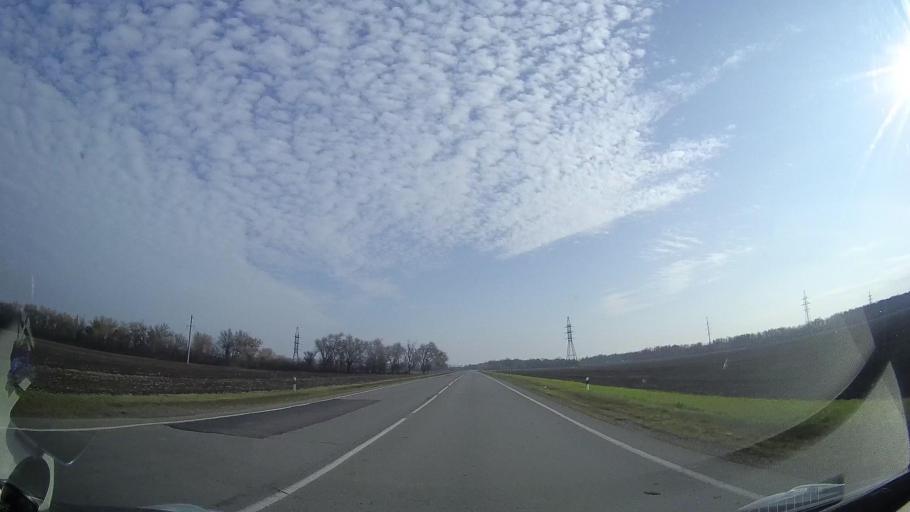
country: RU
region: Rostov
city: Tselina
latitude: 46.5321
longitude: 41.1793
